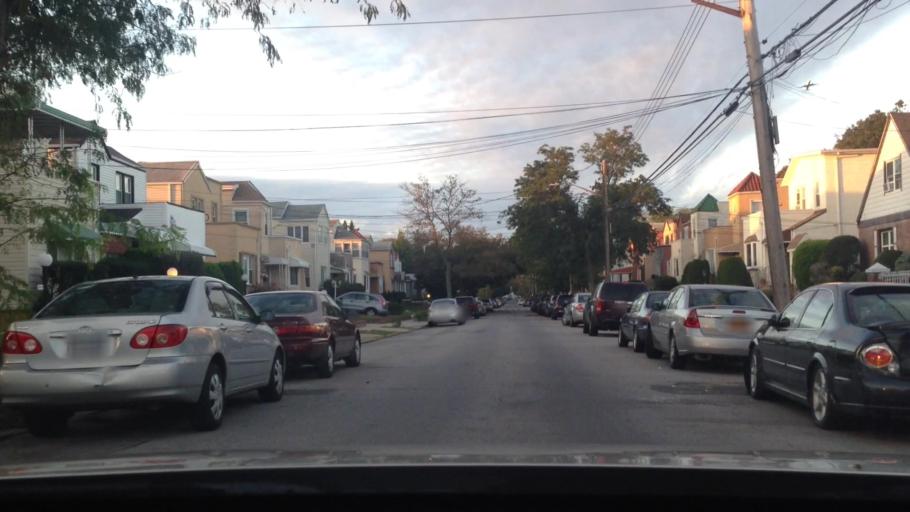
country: US
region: New York
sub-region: Nassau County
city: South Valley Stream
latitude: 40.6714
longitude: -73.7401
